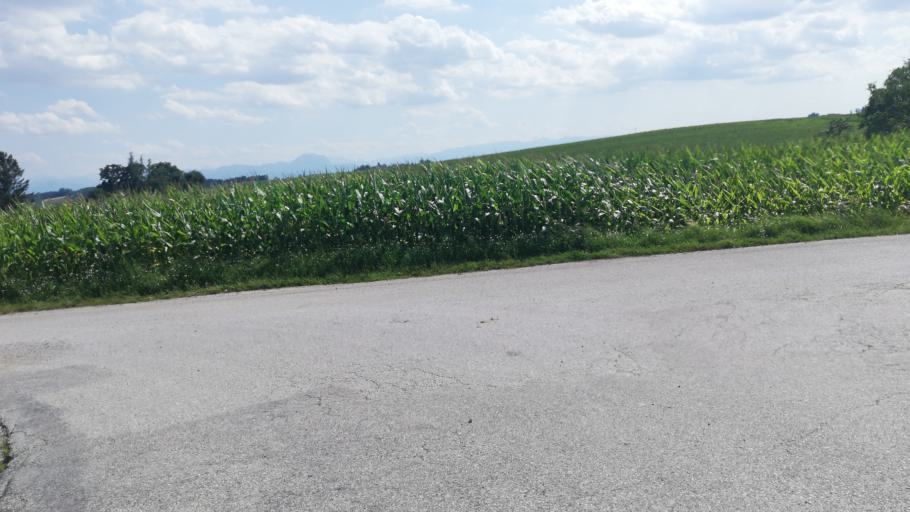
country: AT
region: Upper Austria
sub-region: Wels-Land
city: Pennewang
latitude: 48.1601
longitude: 13.8816
